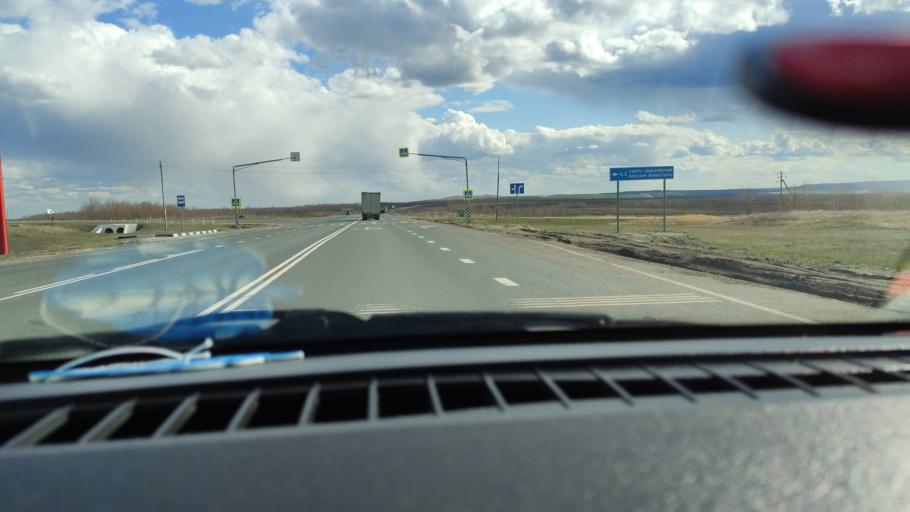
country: RU
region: Saratov
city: Alekseyevka
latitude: 52.2896
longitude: 47.9298
